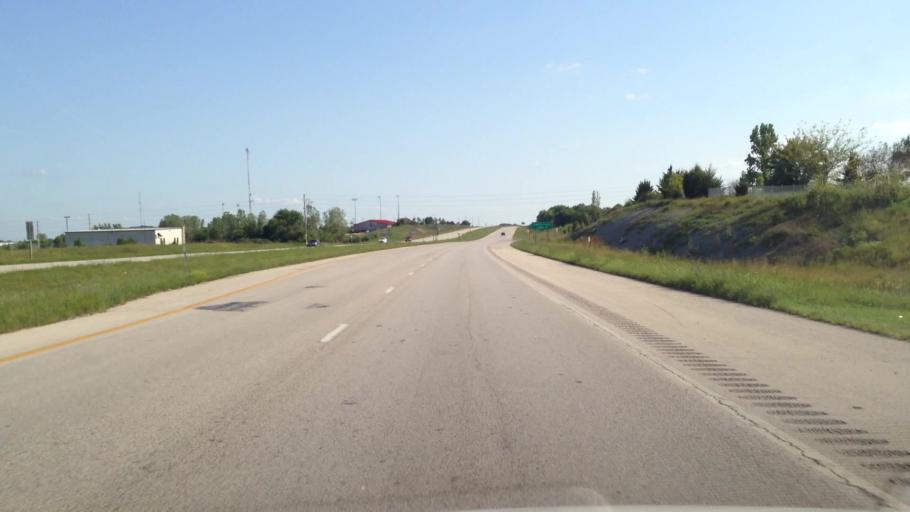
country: US
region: Kansas
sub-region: Bourbon County
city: Fort Scott
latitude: 37.7929
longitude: -94.7049
